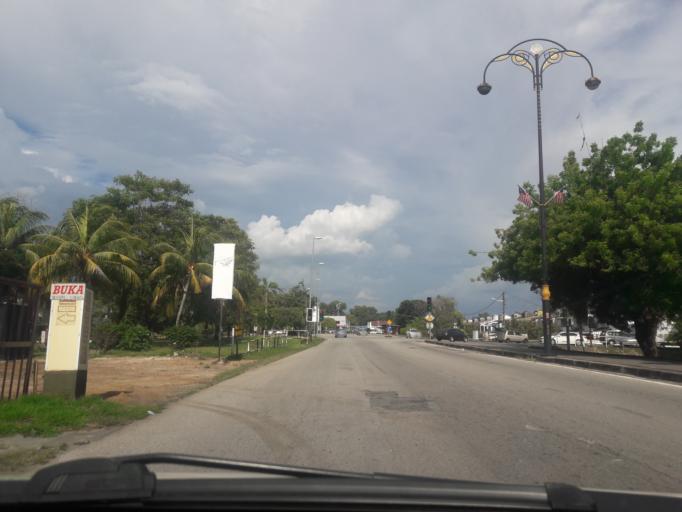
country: MY
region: Kedah
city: Sungai Petani
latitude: 5.6516
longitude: 100.5052
